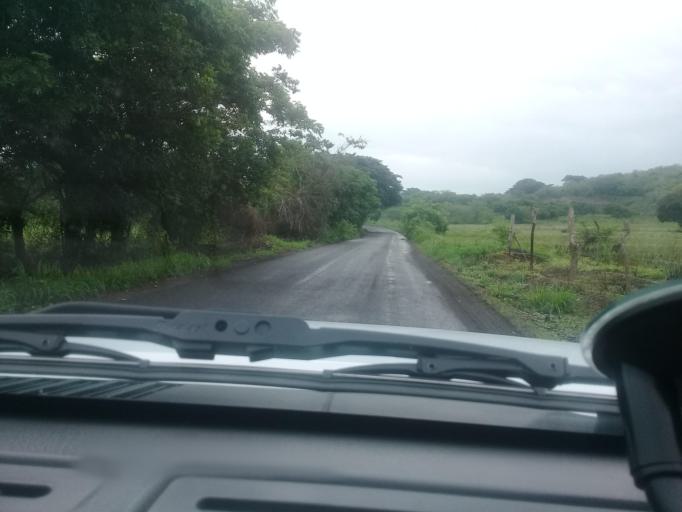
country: MX
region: Veracruz
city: Paso de Ovejas
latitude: 19.2553
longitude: -96.4265
